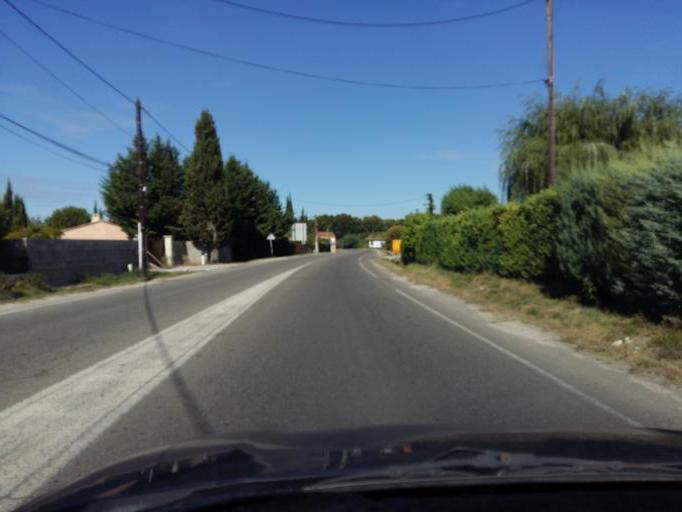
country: FR
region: Provence-Alpes-Cote d'Azur
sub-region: Departement du Vaucluse
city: Mazan
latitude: 44.0582
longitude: 5.1130
